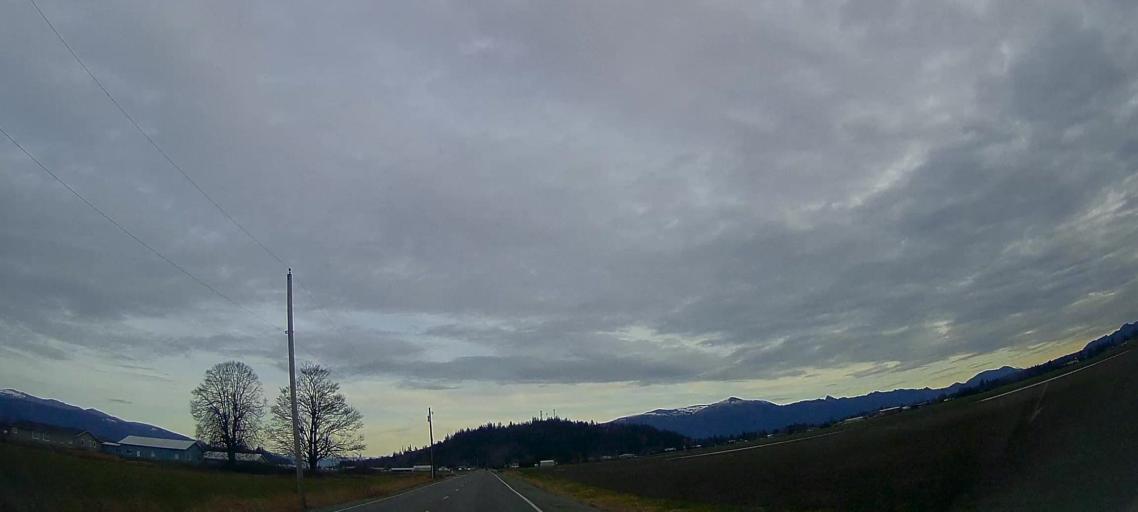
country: US
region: Washington
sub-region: Skagit County
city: Burlington
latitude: 48.4862
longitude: -122.3540
